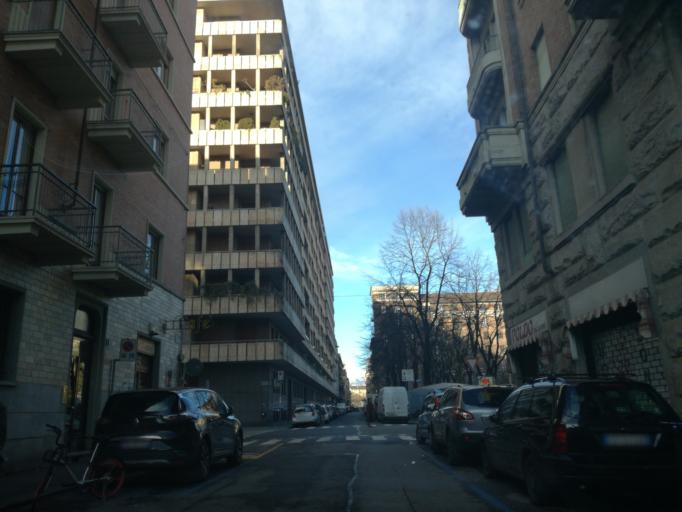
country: IT
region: Piedmont
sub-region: Provincia di Torino
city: Turin
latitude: 45.0729
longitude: 7.6624
